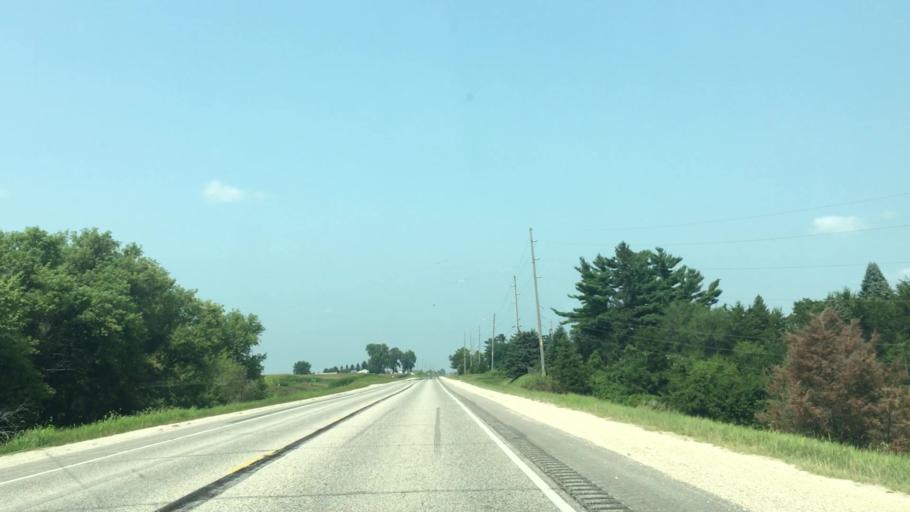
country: US
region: Iowa
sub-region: Fayette County
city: Fayette
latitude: 42.8760
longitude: -91.8105
